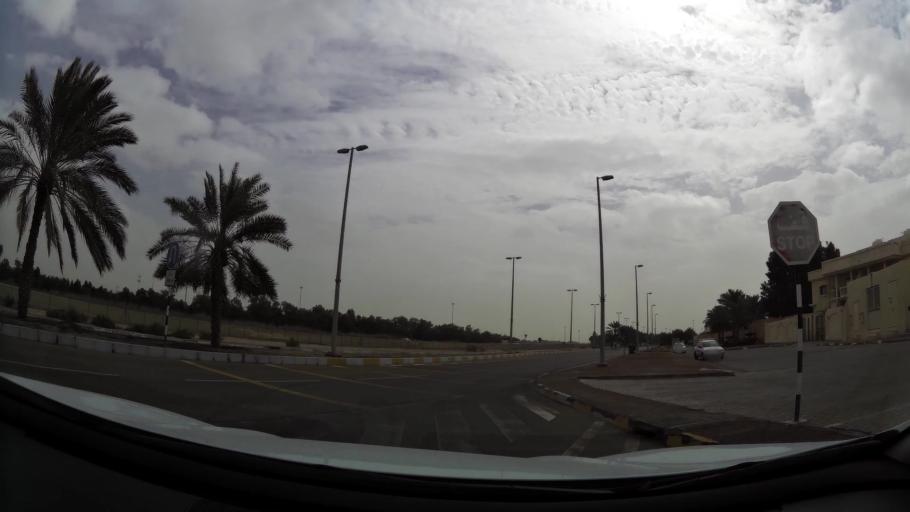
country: AE
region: Abu Dhabi
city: Abu Dhabi
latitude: 24.4046
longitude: 54.5202
